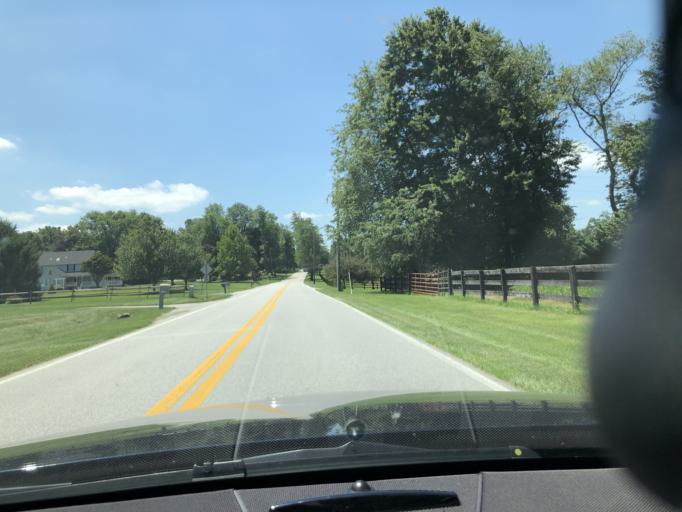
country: US
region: Maryland
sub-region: Carroll County
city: Westminster
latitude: 39.5077
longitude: -76.9399
